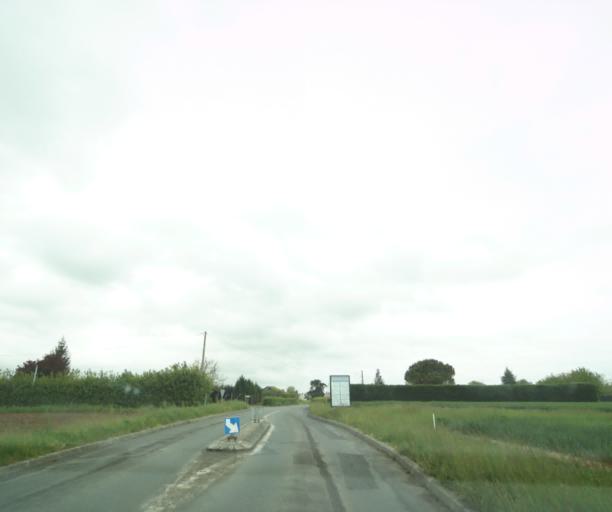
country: FR
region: Poitou-Charentes
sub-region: Departement de la Charente-Maritime
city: Chaniers
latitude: 45.6980
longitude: -0.5409
